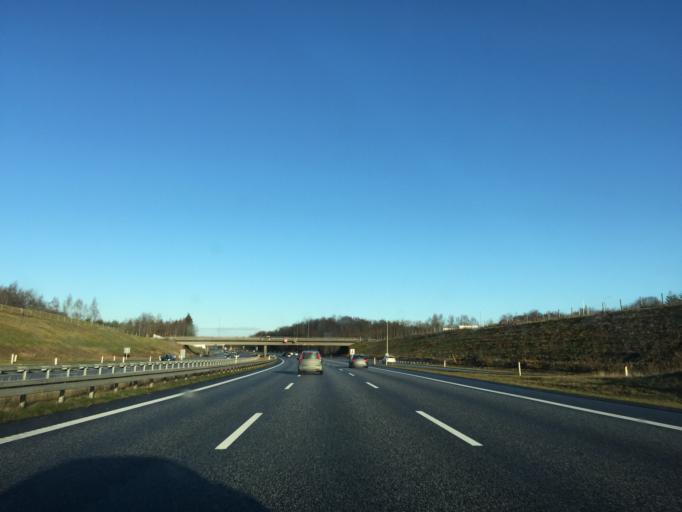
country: DK
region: South Denmark
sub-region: Vejle Kommune
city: Vejle
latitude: 55.6848
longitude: 9.5656
